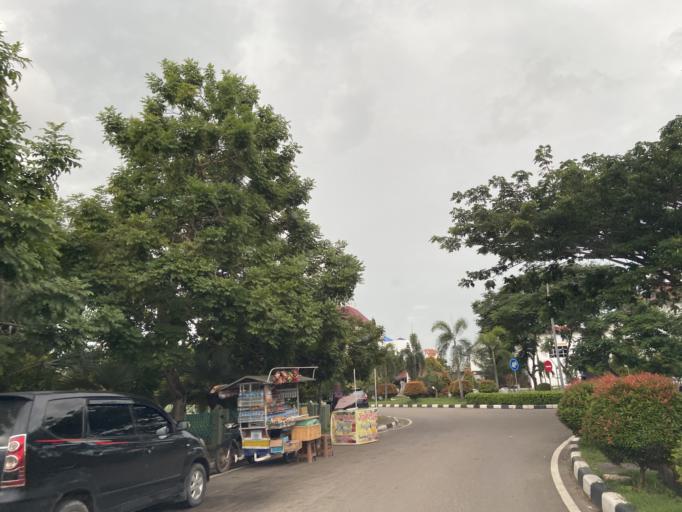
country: SG
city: Singapore
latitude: 1.1261
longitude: 104.0543
